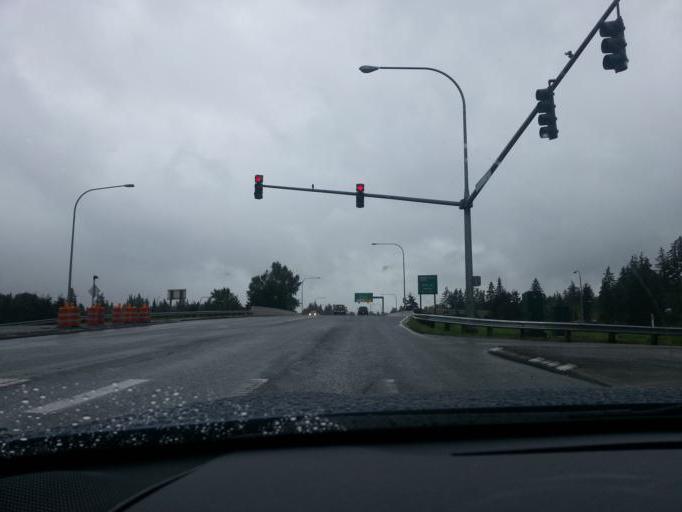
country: US
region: Washington
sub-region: King County
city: Bothell
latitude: 47.7959
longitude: -122.2137
